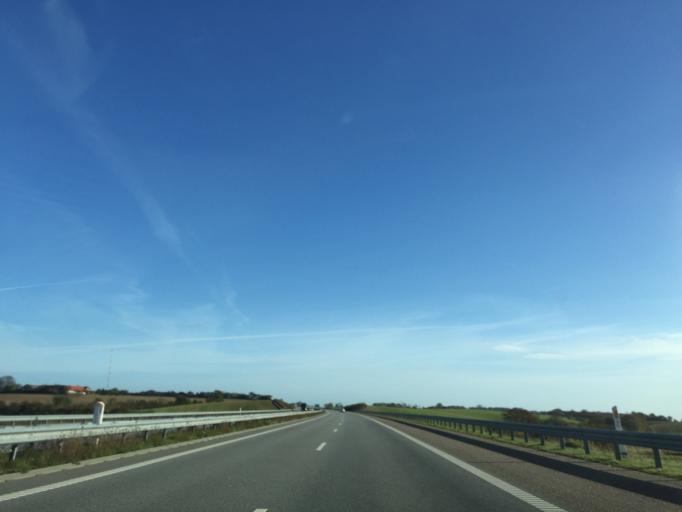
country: DK
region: South Denmark
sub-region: Sonderborg Kommune
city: Grasten
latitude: 54.9536
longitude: 9.5261
